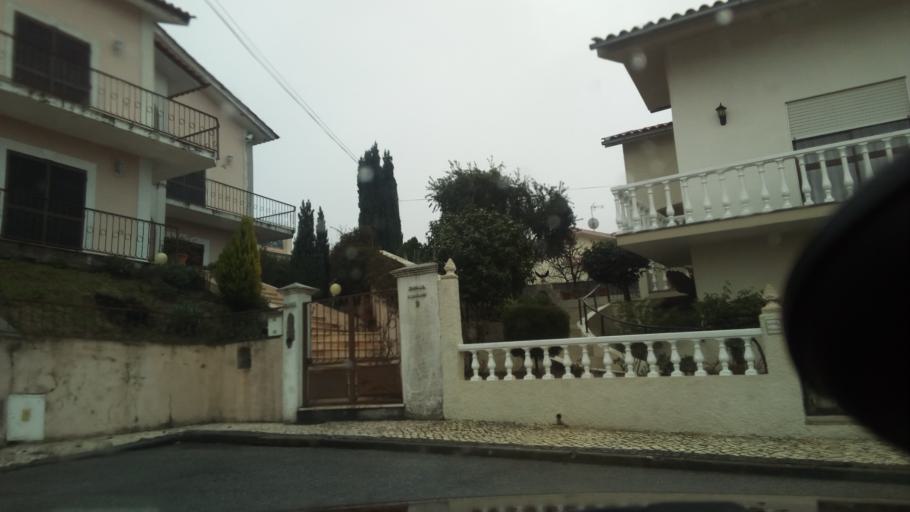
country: PT
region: Viseu
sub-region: Mangualde
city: Mangualde
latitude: 40.6033
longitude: -7.7735
